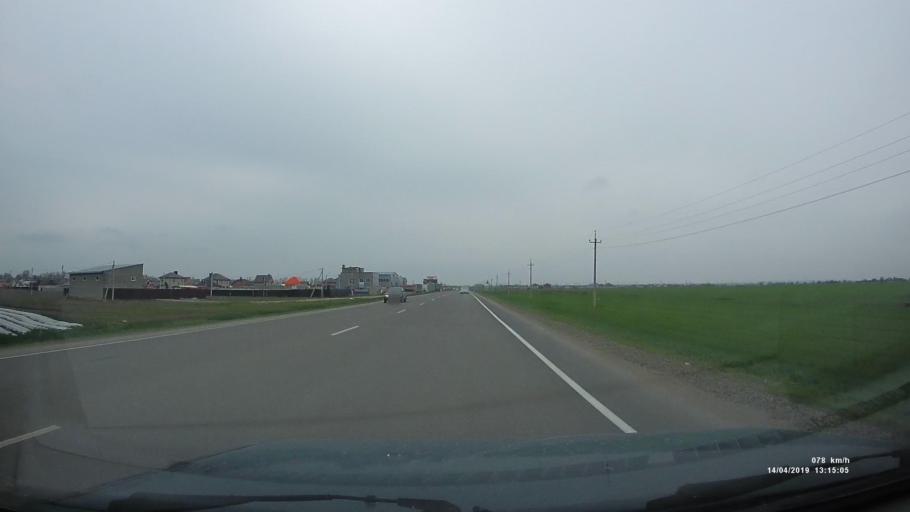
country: RU
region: Rostov
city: Kuleshovka
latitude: 47.0865
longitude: 39.5999
